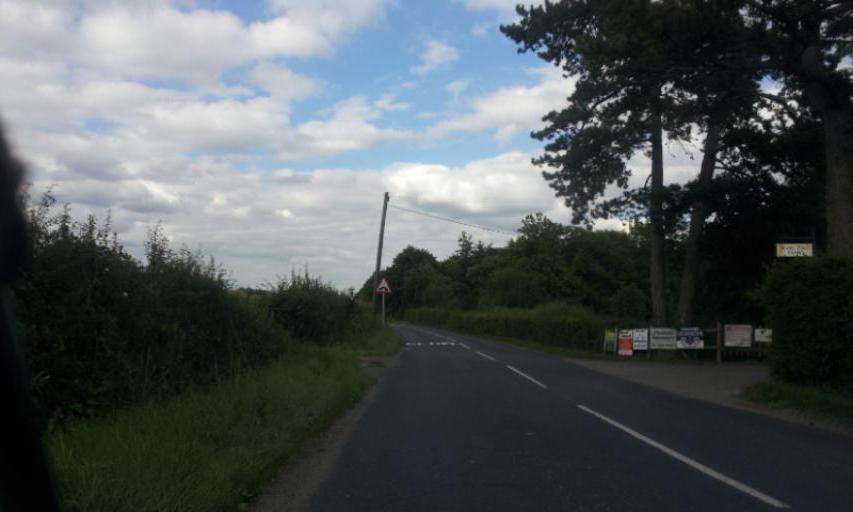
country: GB
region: England
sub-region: Kent
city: Staplehurst
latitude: 51.1683
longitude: 0.5674
